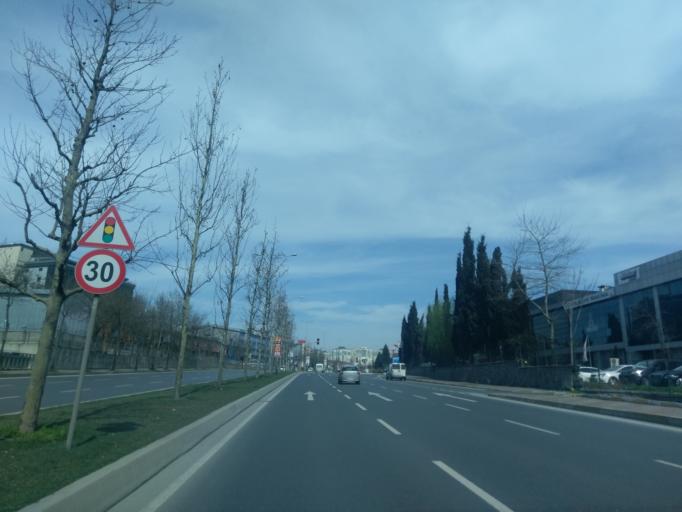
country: TR
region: Istanbul
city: Basaksehir
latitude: 41.0941
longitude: 28.7949
